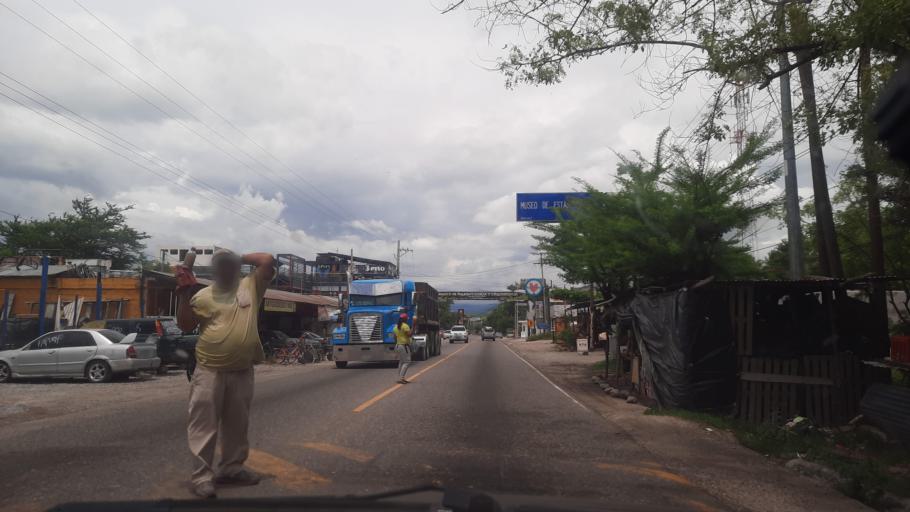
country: GT
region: Zacapa
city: Estanzuela
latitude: 15.0035
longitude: -89.5710
